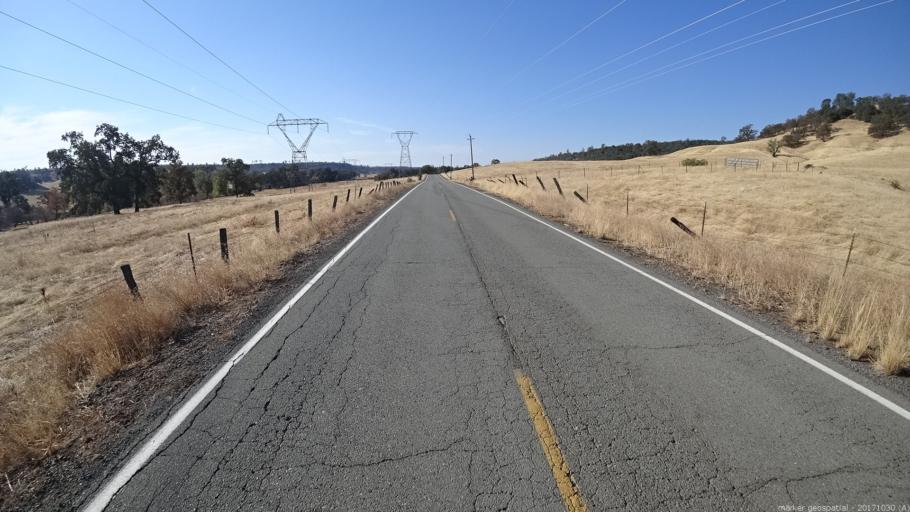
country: US
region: California
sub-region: Shasta County
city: Bella Vista
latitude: 40.6395
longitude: -122.0878
